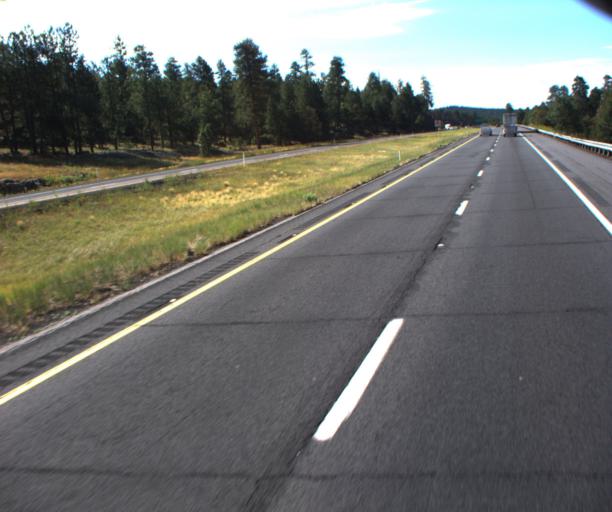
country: US
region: Arizona
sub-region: Coconino County
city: Mountainaire
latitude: 35.0609
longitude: -111.6854
